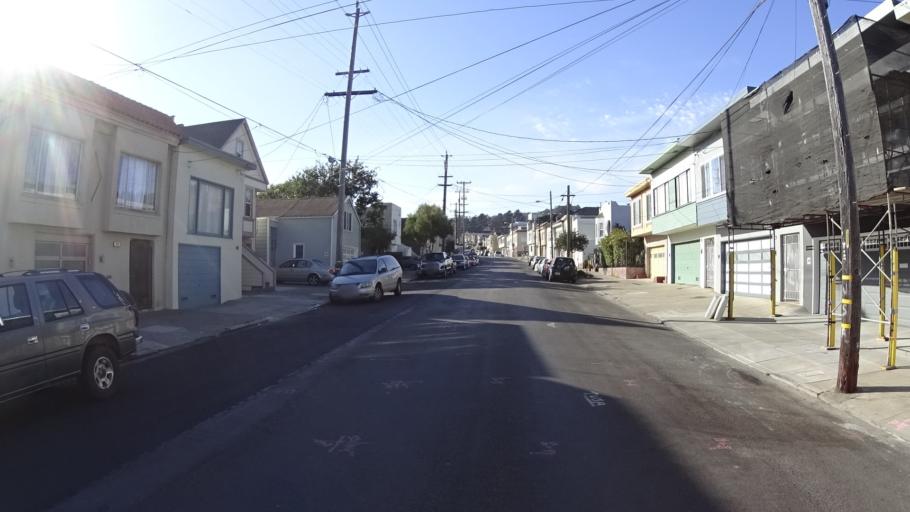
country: US
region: California
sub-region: San Mateo County
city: Brisbane
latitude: 37.7127
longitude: -122.4057
